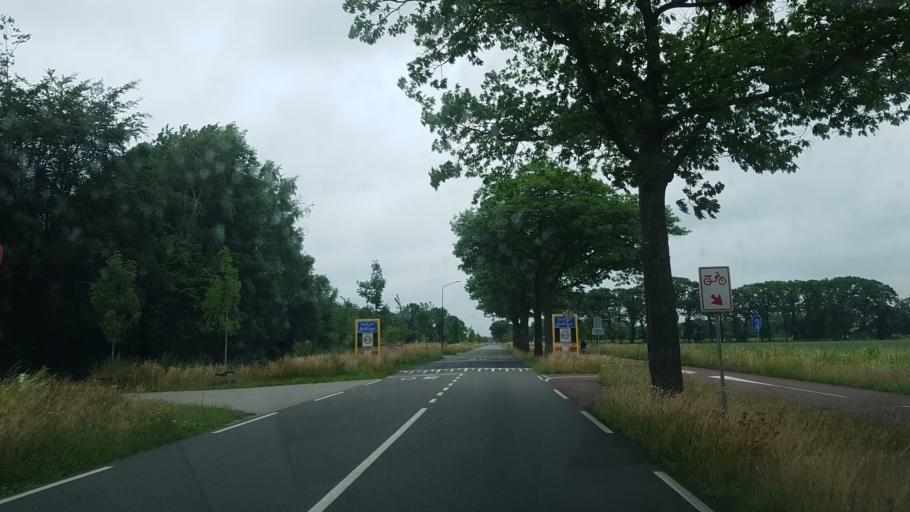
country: NL
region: North Brabant
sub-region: Gemeente Son en Breugel
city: Son
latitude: 51.5357
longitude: 5.4876
